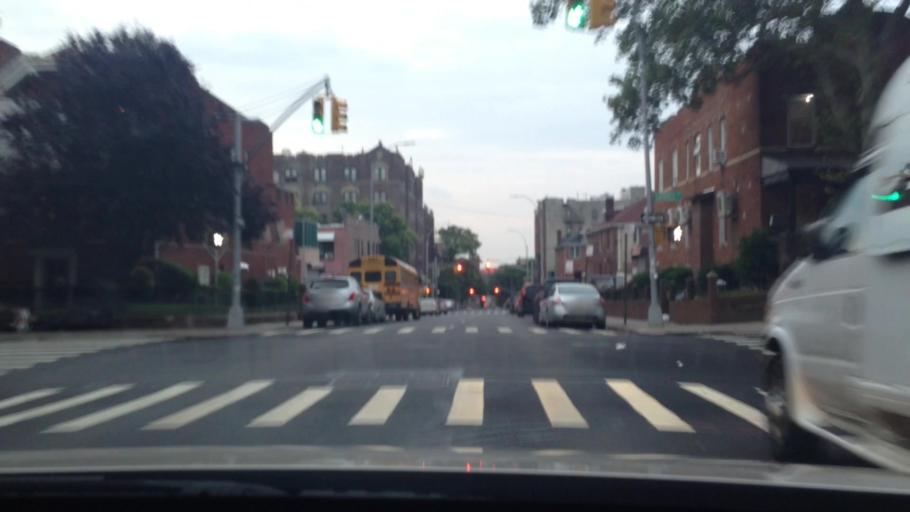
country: US
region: New York
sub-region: Kings County
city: Brooklyn
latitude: 40.6666
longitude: -73.9339
